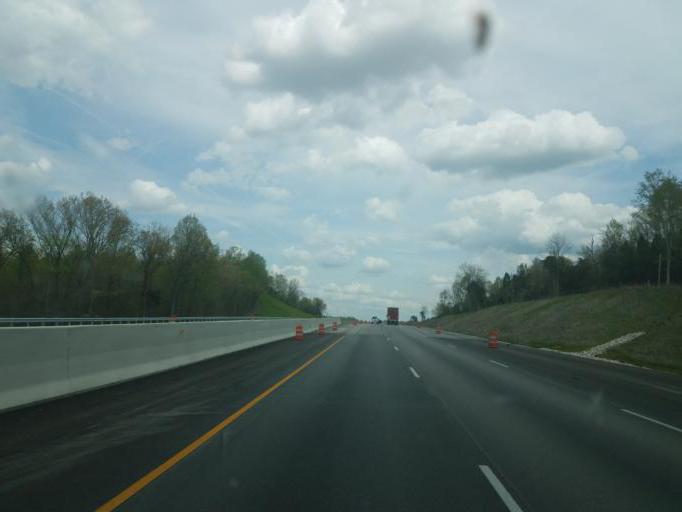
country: US
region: Kentucky
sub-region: Hart County
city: Munfordville
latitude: 37.3671
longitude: -85.8927
